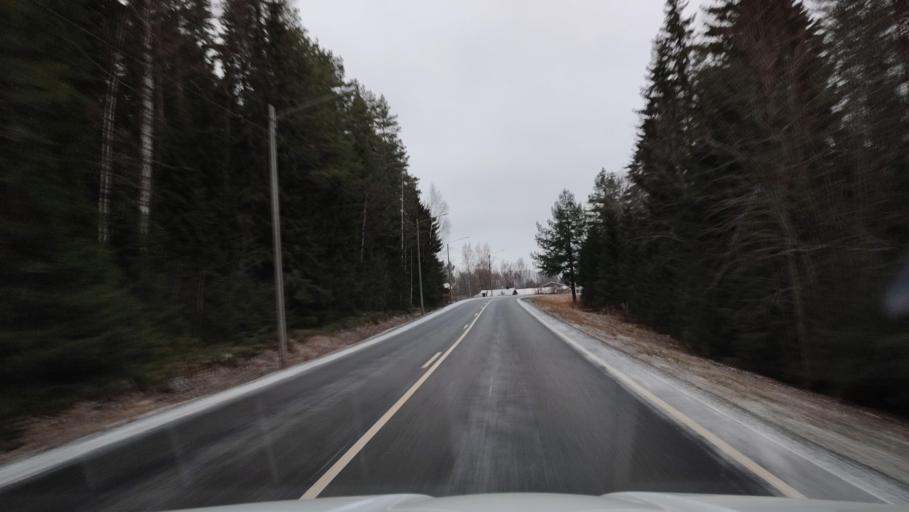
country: FI
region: Southern Ostrobothnia
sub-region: Suupohja
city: Karijoki
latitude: 62.2996
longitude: 21.6834
